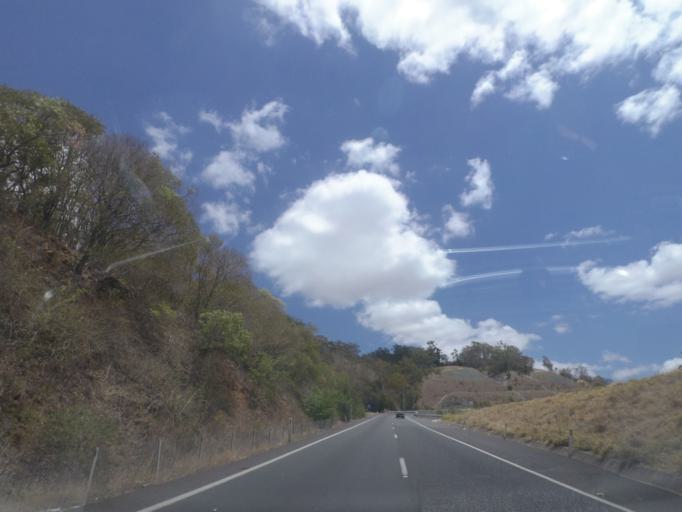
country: AU
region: Queensland
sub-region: Toowoomba
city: East Toowoomba
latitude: -27.5723
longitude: 151.9831
